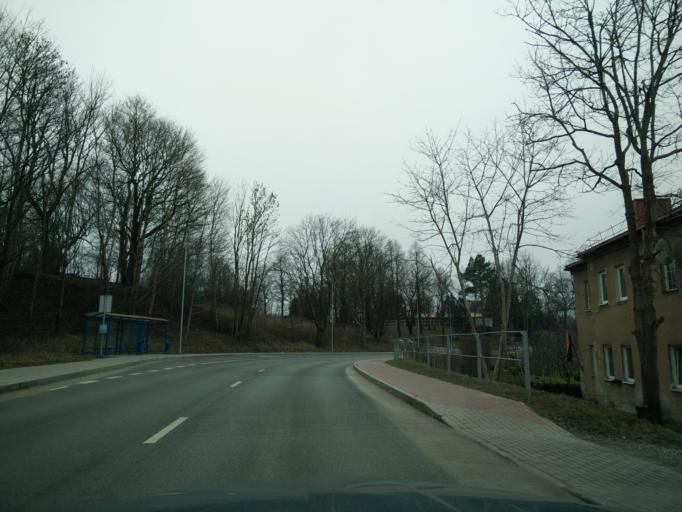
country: LT
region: Klaipedos apskritis
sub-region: Klaipeda
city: Klaipeda
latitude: 55.7163
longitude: 21.1669
